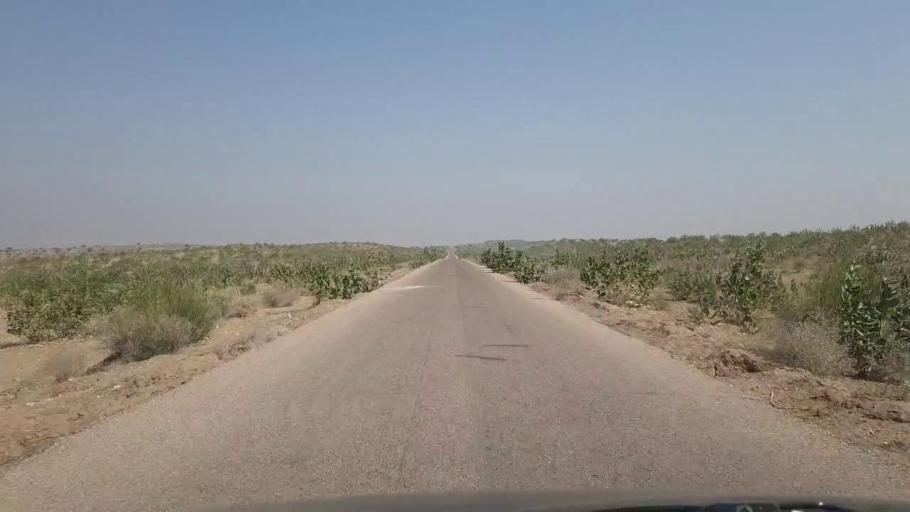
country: PK
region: Sindh
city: Chor
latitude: 25.6744
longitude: 70.1709
